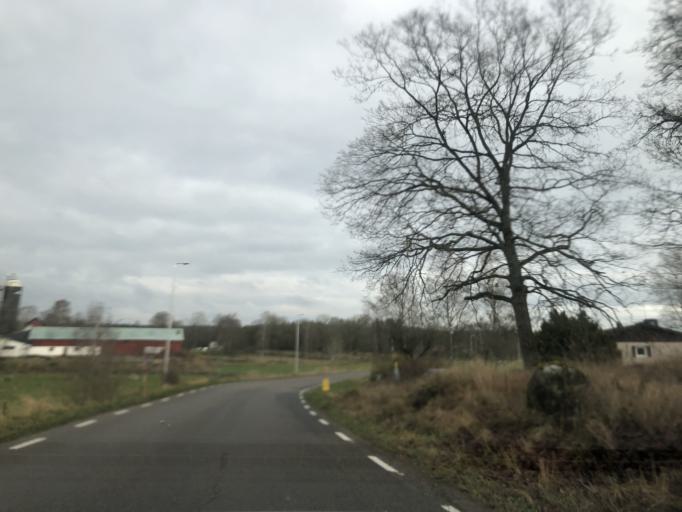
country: SE
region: Vaestra Goetaland
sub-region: Boras Kommun
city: Dalsjofors
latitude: 57.8285
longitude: 13.1665
